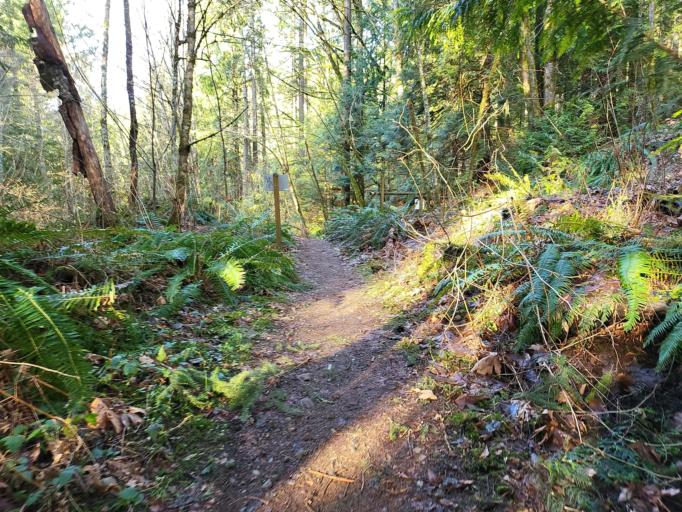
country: US
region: Washington
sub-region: King County
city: Issaquah
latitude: 47.5234
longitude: -122.0236
